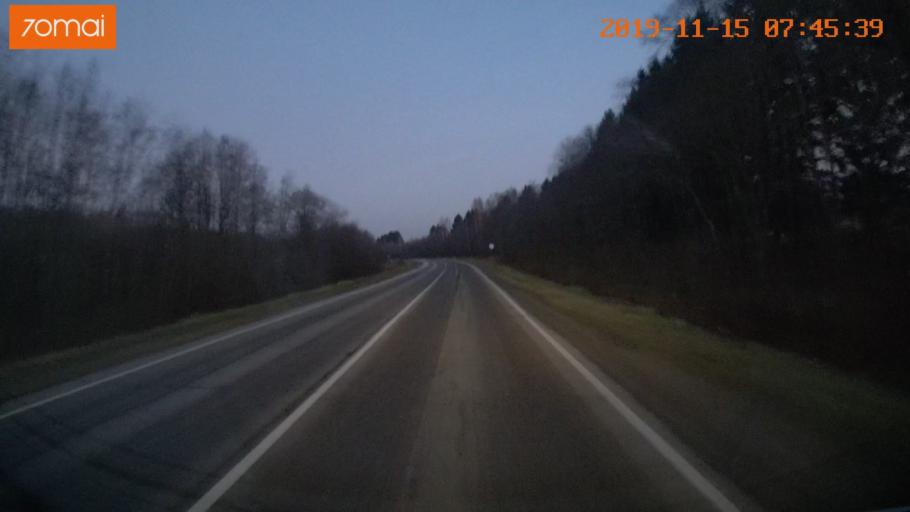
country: RU
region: Vologda
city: Sheksna
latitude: 58.8248
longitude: 38.2965
